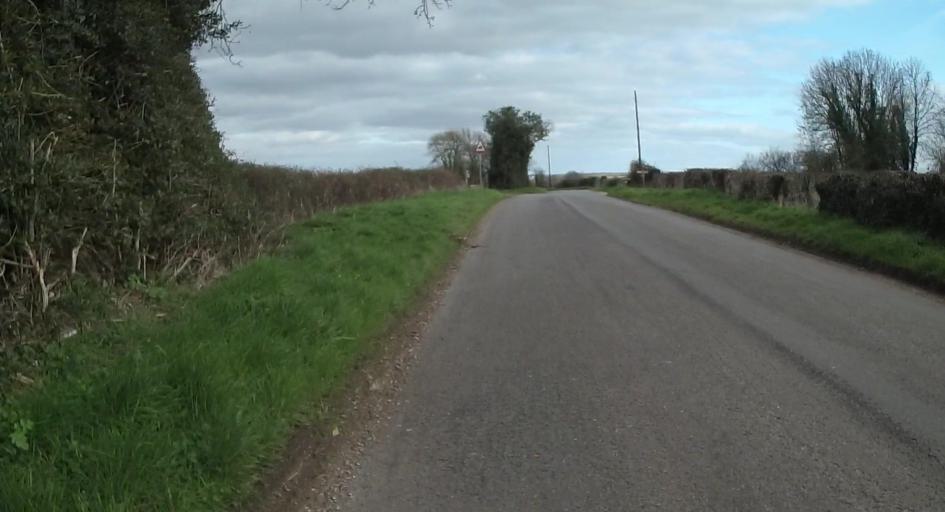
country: GB
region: England
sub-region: Hampshire
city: Andover
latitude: 51.1560
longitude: -1.4739
